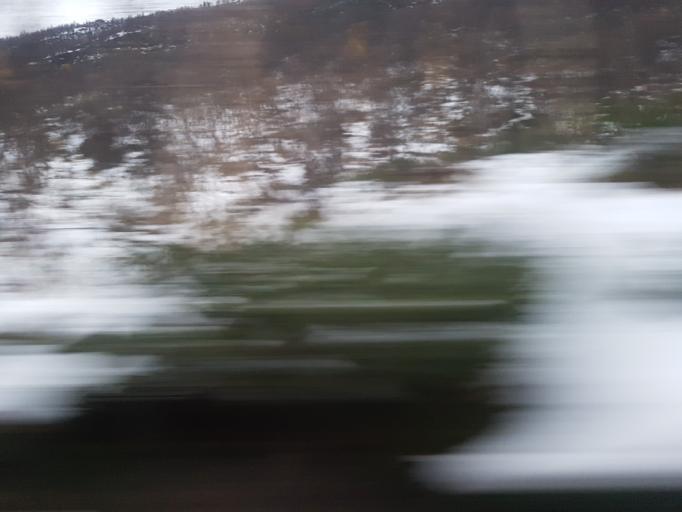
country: NO
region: Sor-Trondelag
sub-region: Oppdal
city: Oppdal
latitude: 62.3468
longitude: 9.6262
